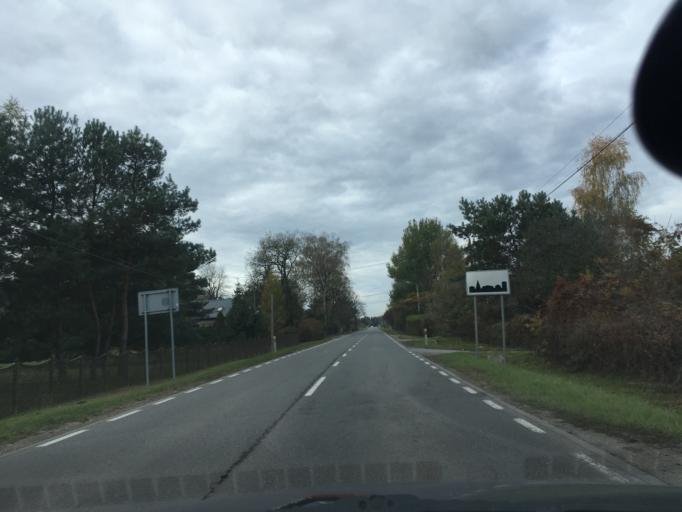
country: PL
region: Masovian Voivodeship
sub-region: Powiat piaseczynski
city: Tarczyn
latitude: 51.9788
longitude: 20.8640
